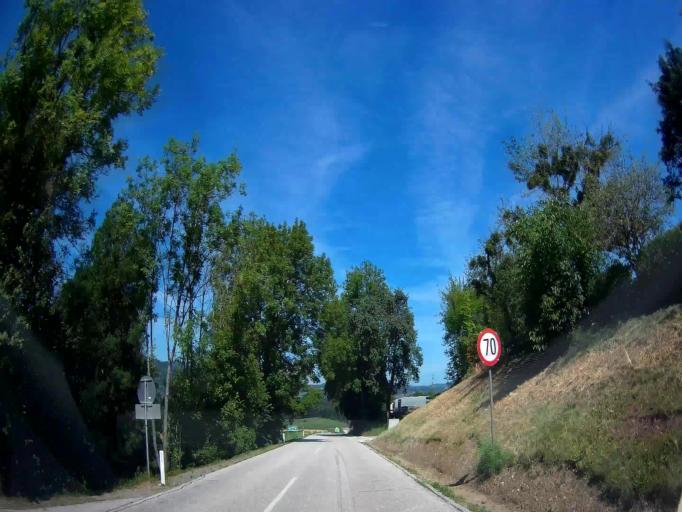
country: AT
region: Carinthia
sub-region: Politischer Bezirk Sankt Veit an der Glan
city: St. Georgen am Laengsee
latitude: 46.8016
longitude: 14.4124
